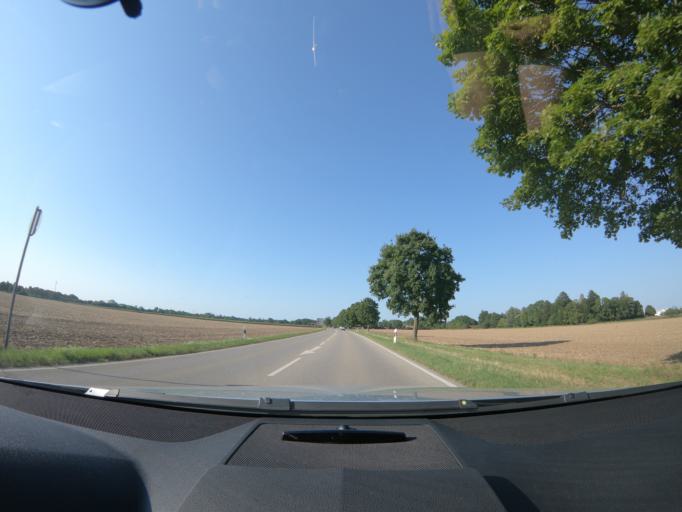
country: DE
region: Bavaria
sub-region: Upper Bavaria
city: Unterhaching
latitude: 48.0852
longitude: 11.6234
